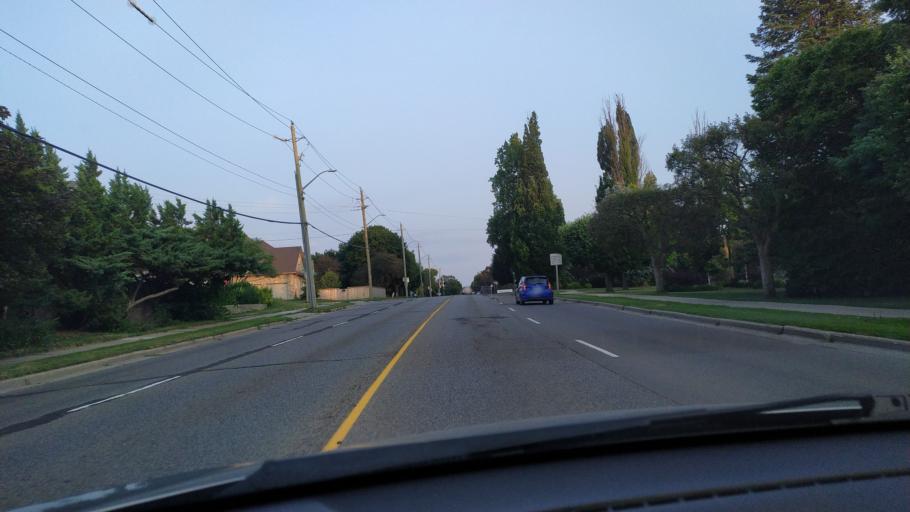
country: CA
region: Ontario
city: Waterloo
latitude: 43.4557
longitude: -80.5289
